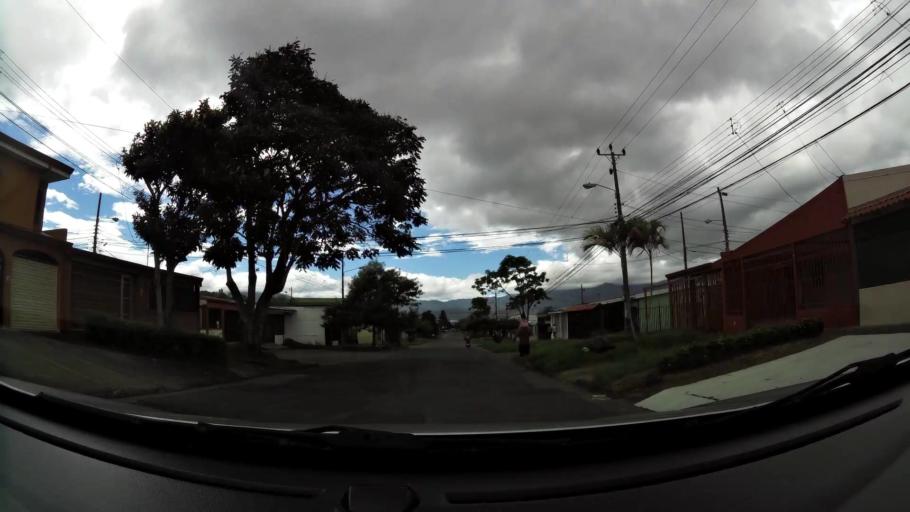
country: CR
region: San Jose
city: Curridabat
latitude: 9.9214
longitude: -84.0388
